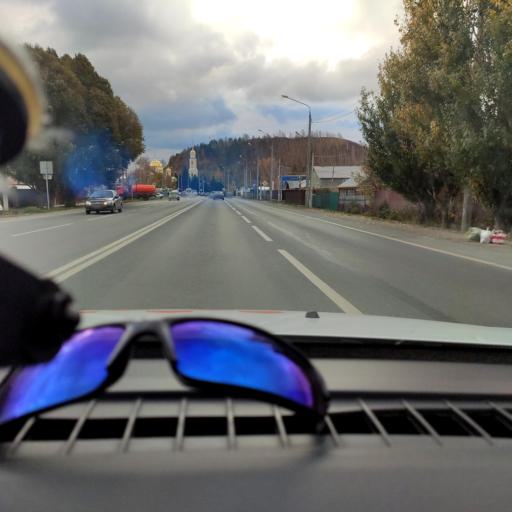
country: RU
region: Samara
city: Volzhskiy
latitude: 53.4283
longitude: 50.1199
